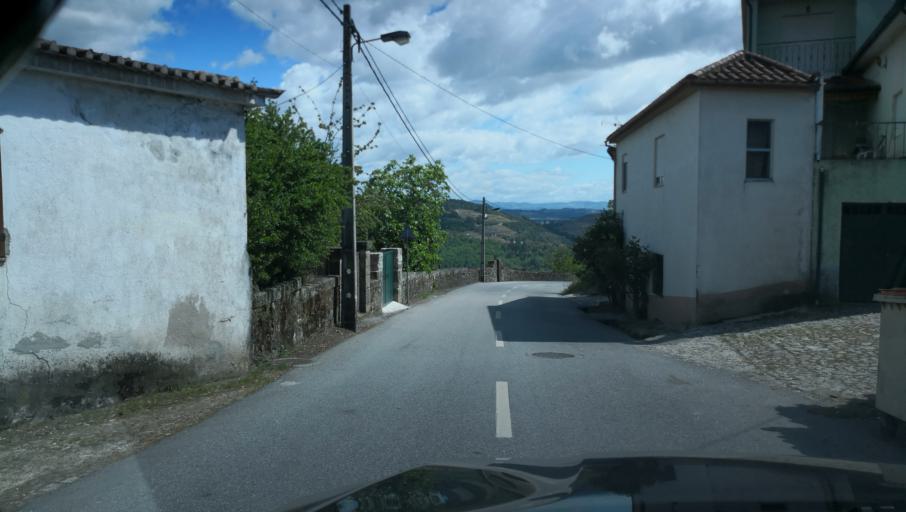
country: PT
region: Vila Real
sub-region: Vila Real
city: Vila Real
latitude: 41.2571
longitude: -7.7337
